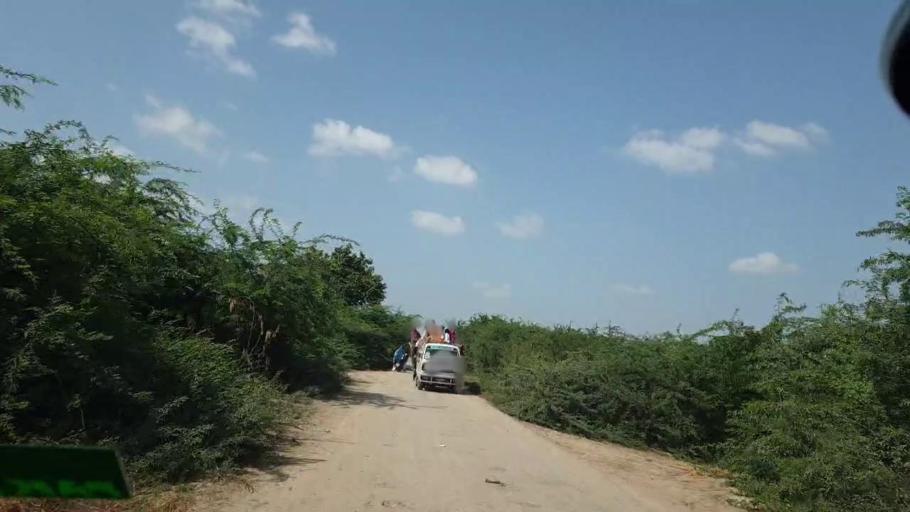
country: PK
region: Sindh
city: Naukot
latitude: 24.6391
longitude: 69.2273
